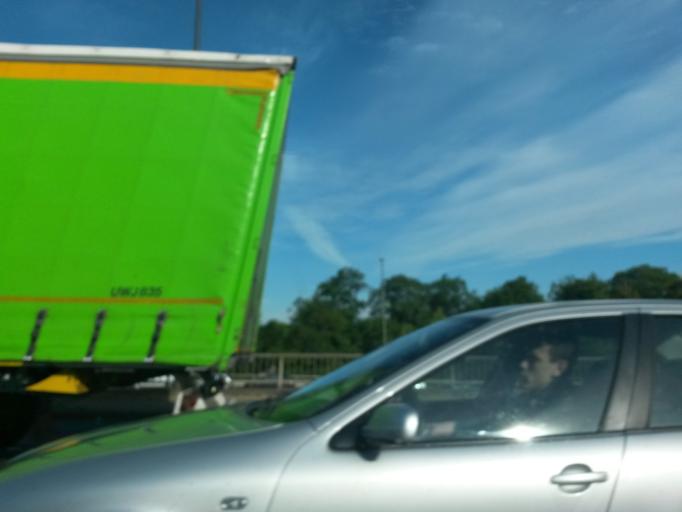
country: DE
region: Bavaria
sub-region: Regierungsbezirk Unterfranken
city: Wuerzburg
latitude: 49.7952
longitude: 9.9516
